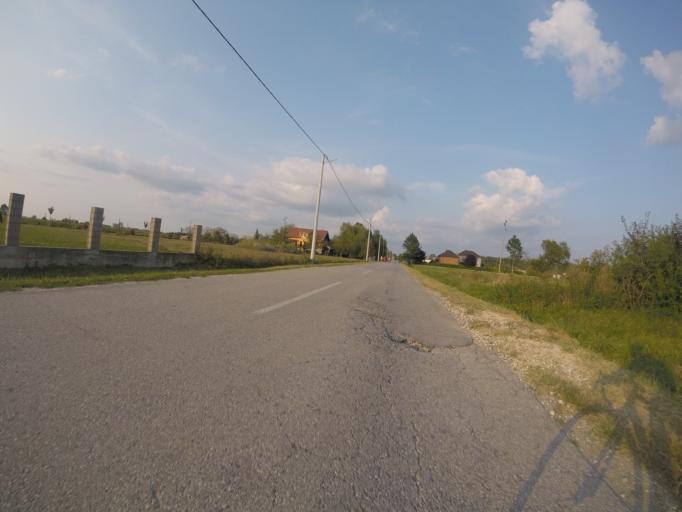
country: HR
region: Zagrebacka
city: Kuce
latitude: 45.7189
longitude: 16.2006
